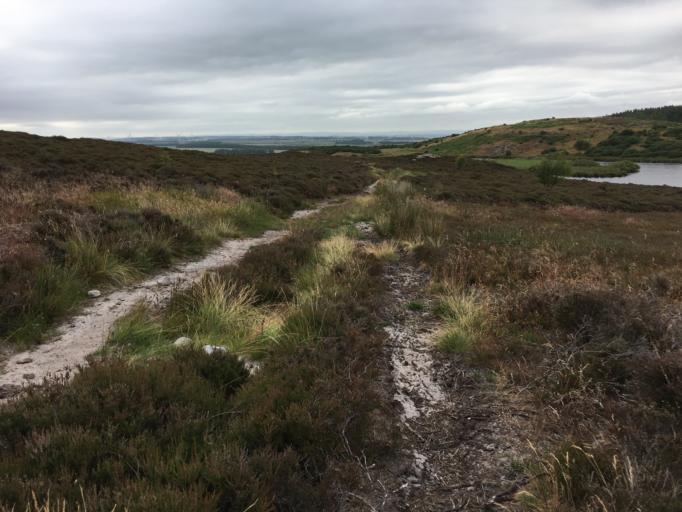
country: GB
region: England
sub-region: Northumberland
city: Lowick
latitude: 55.6198
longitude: -1.9191
